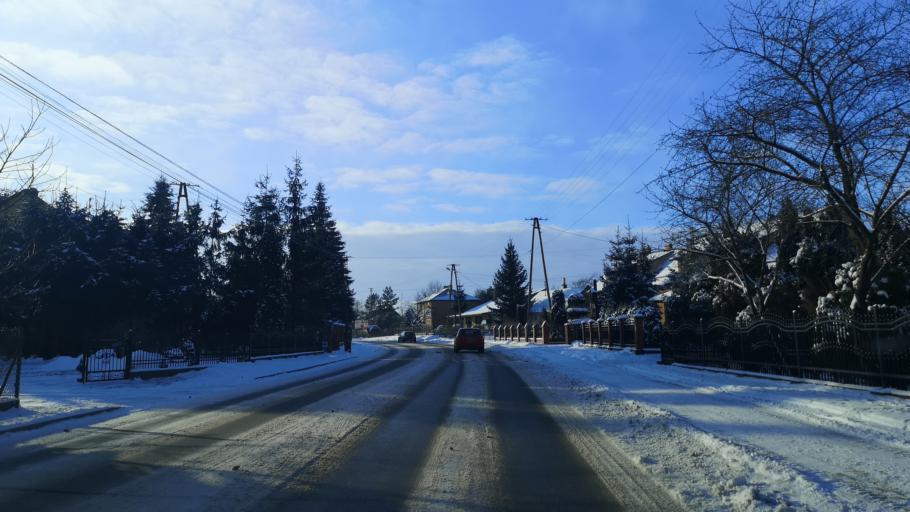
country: PL
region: Subcarpathian Voivodeship
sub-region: Powiat przeworski
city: Gorliczyna
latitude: 50.0933
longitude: 22.4917
